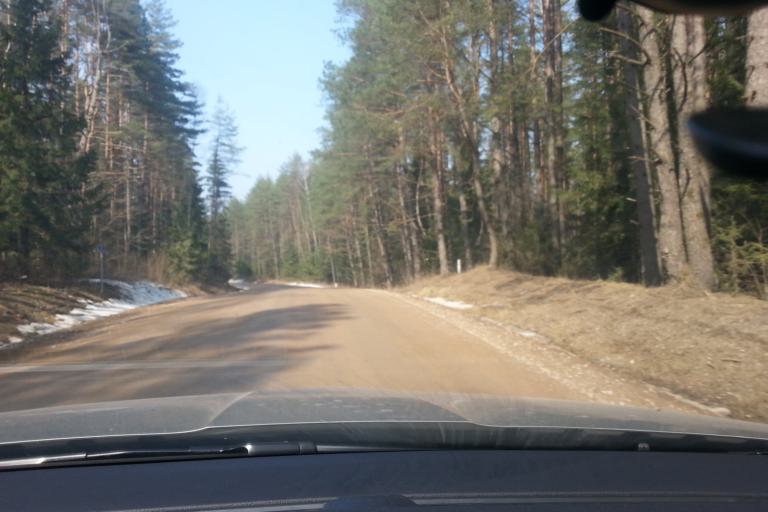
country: LT
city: Trakai
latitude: 54.5642
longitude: 24.9759
